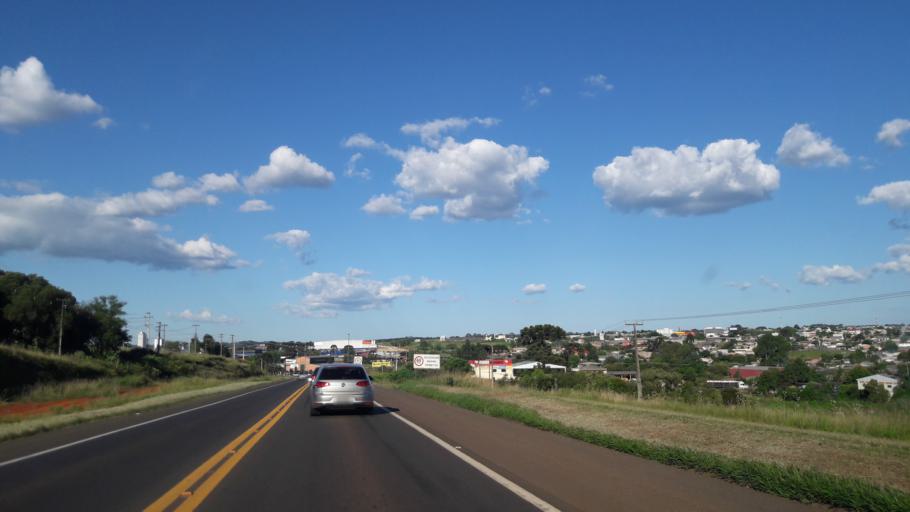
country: BR
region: Parana
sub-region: Guarapuava
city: Guarapuava
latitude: -25.3692
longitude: -51.4959
